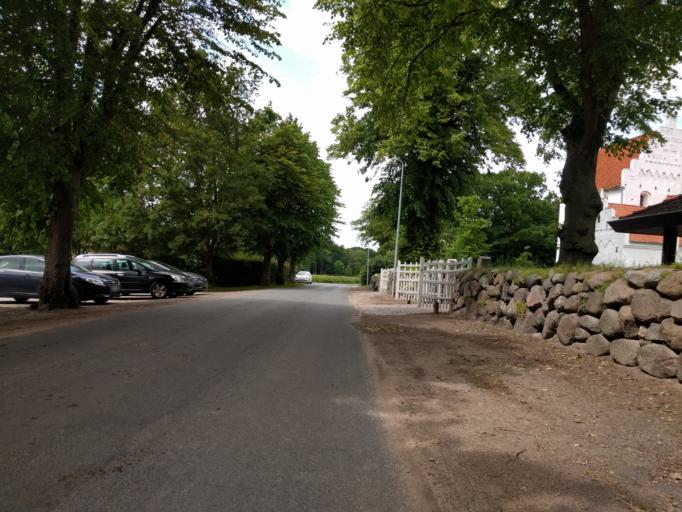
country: DK
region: South Denmark
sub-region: Odense Kommune
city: Bullerup
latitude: 55.4274
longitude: 10.4921
